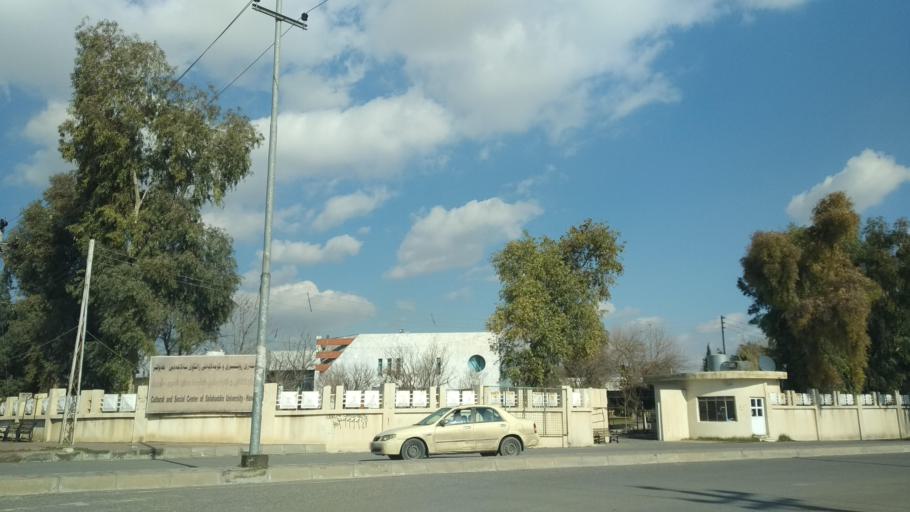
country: IQ
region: Arbil
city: Erbil
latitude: 36.1418
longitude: 44.0207
